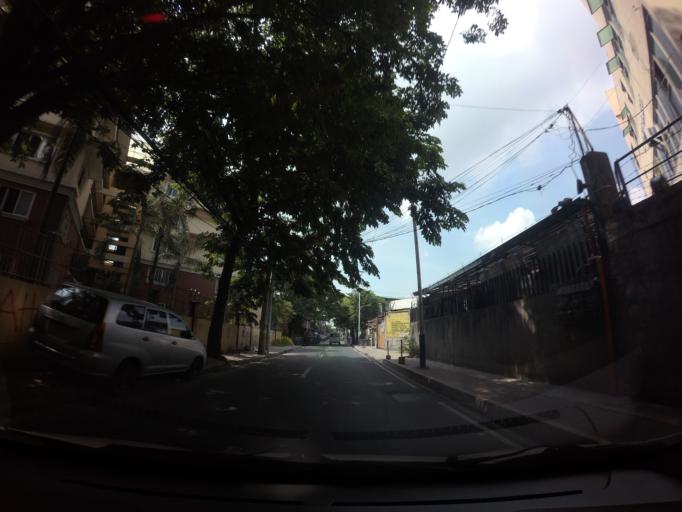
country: PH
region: Calabarzon
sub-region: Province of Rizal
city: Pateros
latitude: 14.5304
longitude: 121.0724
